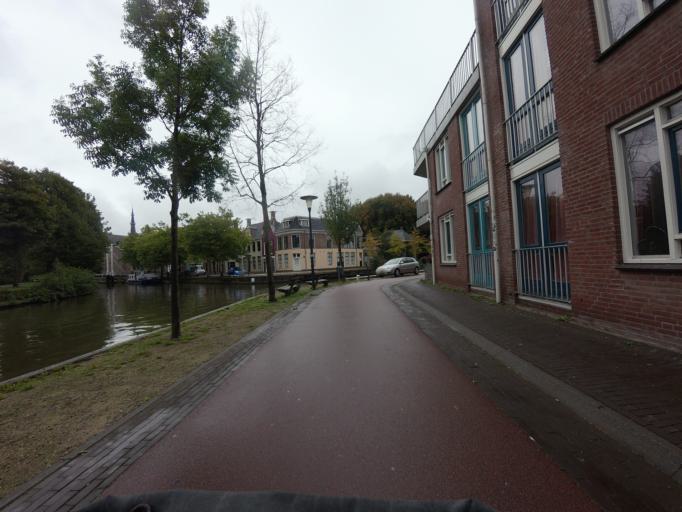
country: NL
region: Friesland
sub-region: Gemeente Leeuwarden
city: Bilgaard
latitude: 53.2073
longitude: 5.7979
